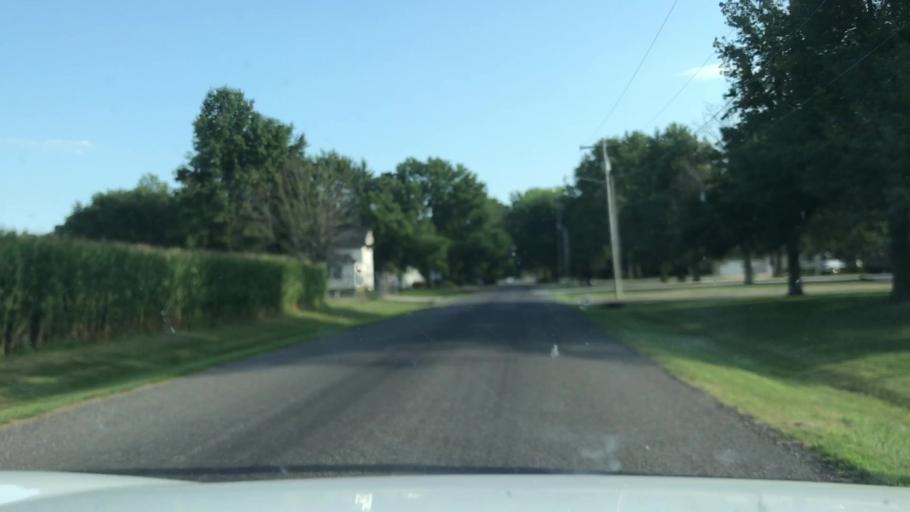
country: US
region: Illinois
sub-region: Washington County
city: Okawville
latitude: 38.3957
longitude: -89.4866
